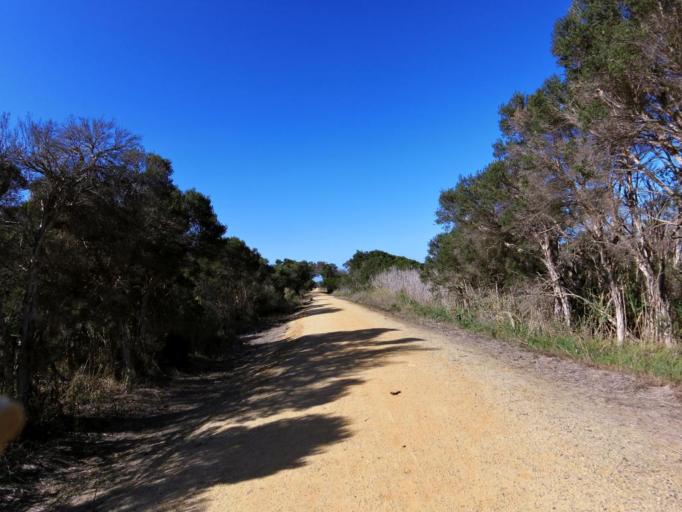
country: AU
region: Victoria
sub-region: Bass Coast
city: North Wonthaggi
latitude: -38.5803
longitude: 145.5525
